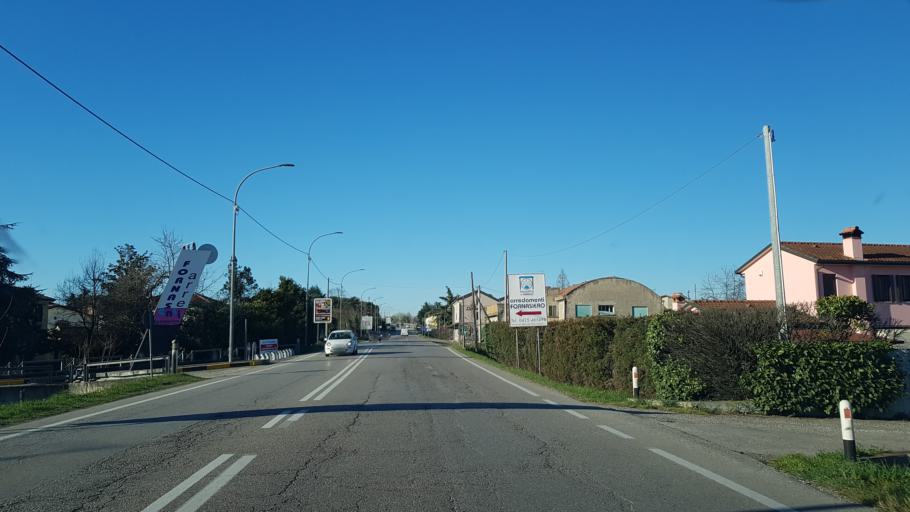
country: IT
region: Veneto
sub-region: Provincia di Padova
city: Boara Pisani
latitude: 45.0996
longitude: 11.7856
